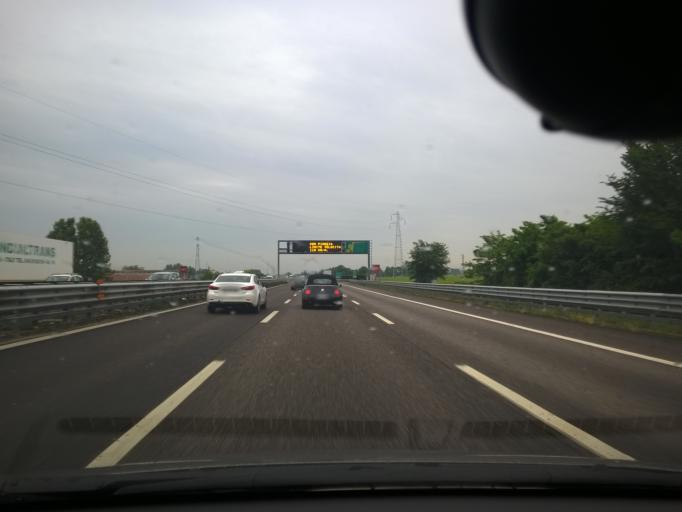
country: IT
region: Lombardy
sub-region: Provincia di Brescia
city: San Martino della Battaglia
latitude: 45.4355
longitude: 10.5929
